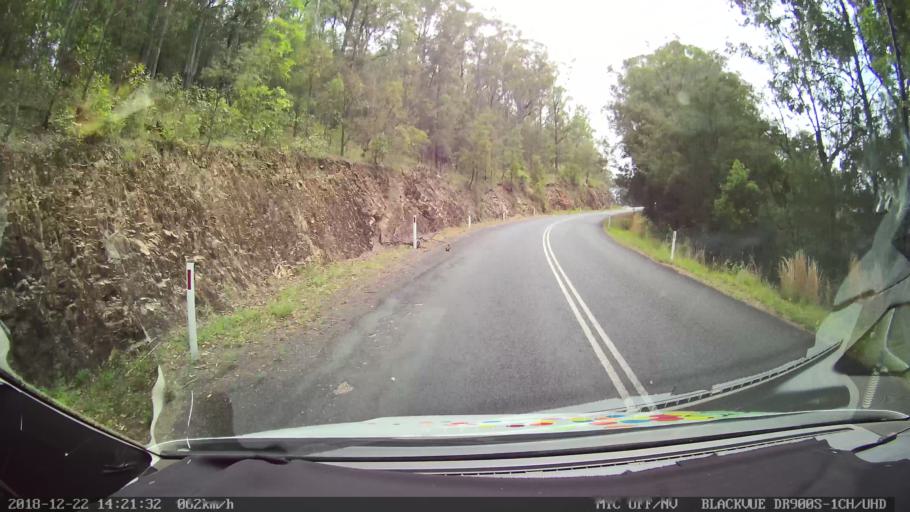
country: AU
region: New South Wales
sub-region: Clarence Valley
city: Coutts Crossing
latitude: -30.0212
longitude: 152.6579
